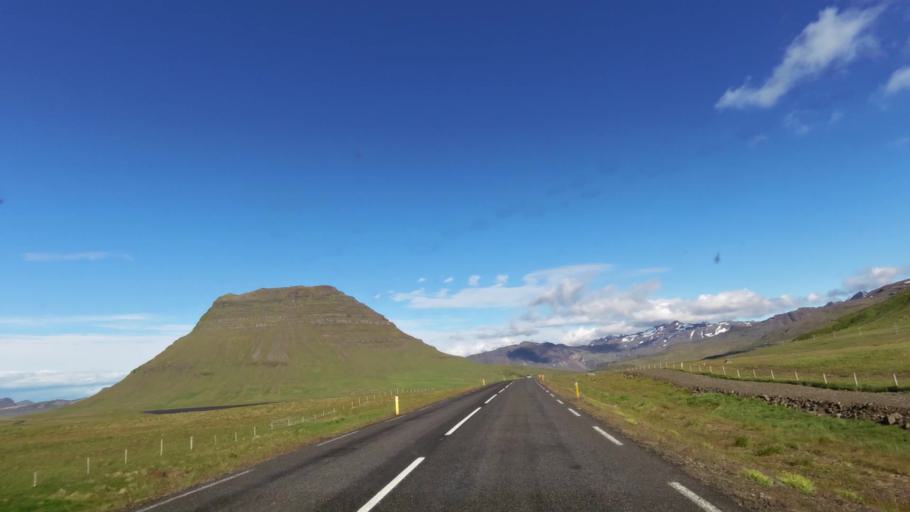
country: IS
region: West
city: Olafsvik
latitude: 64.9398
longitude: -23.3640
